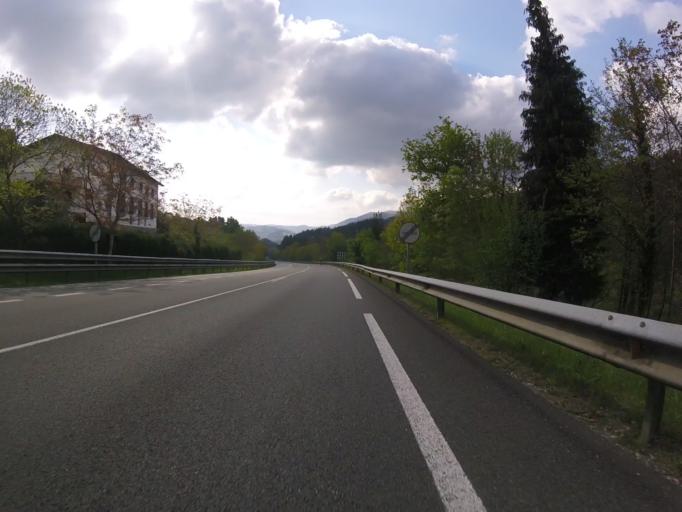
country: ES
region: Basque Country
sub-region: Provincia de Guipuzcoa
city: Azkoitia
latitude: 43.1941
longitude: -2.3362
